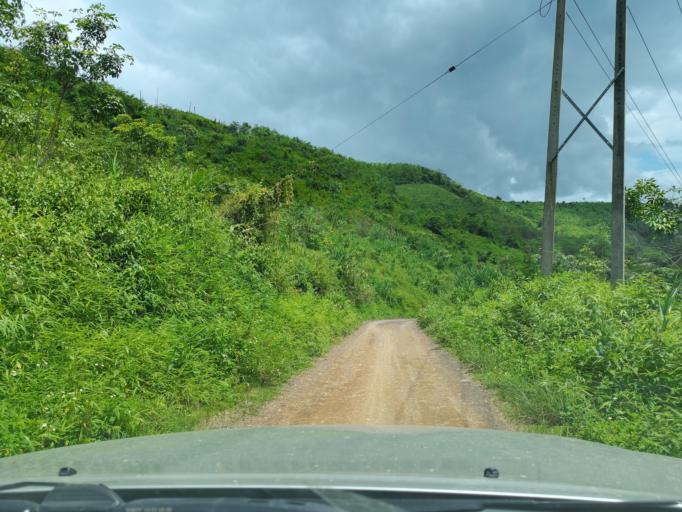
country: LA
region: Loungnamtha
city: Muang Long
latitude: 20.7169
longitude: 101.0146
